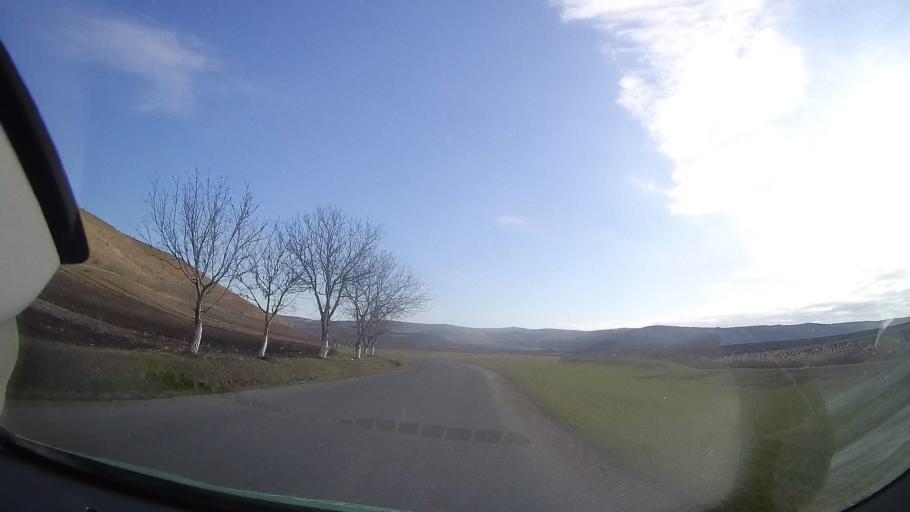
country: RO
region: Mures
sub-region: Comuna Valea Larga
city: Valea Larga
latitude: 46.6046
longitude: 24.0969
